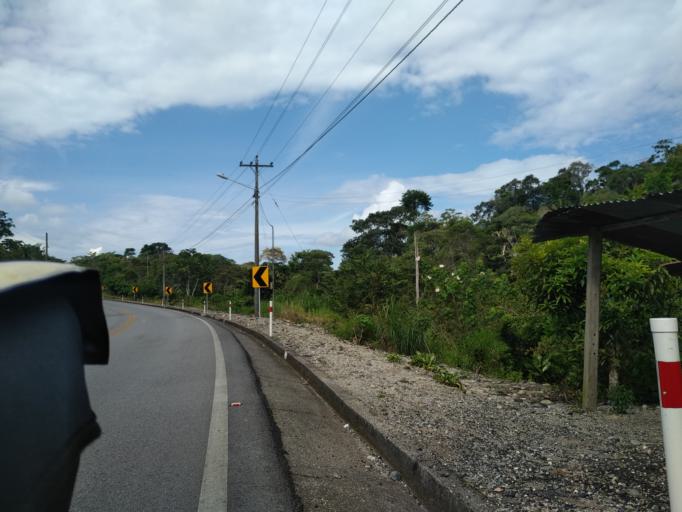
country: EC
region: Napo
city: Tena
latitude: -1.0915
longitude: -77.7912
